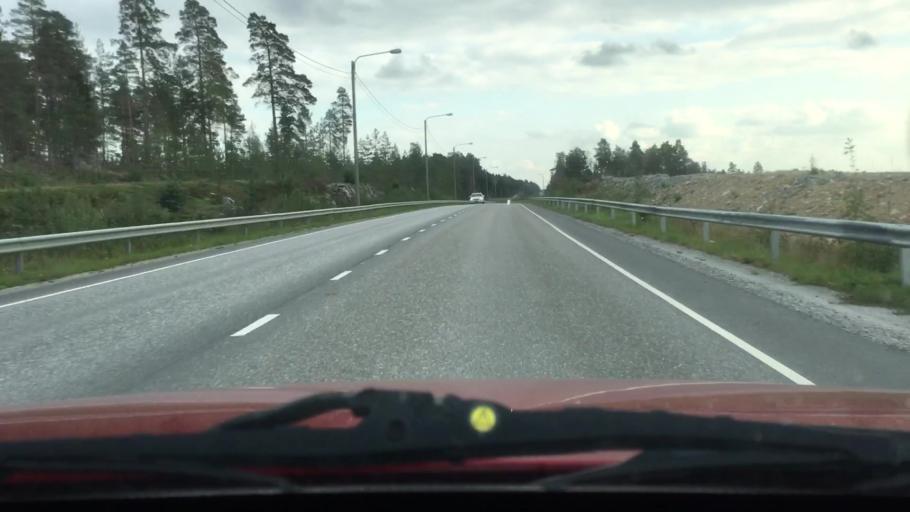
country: FI
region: Varsinais-Suomi
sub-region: Turku
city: Masku
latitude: 60.5465
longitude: 22.1271
